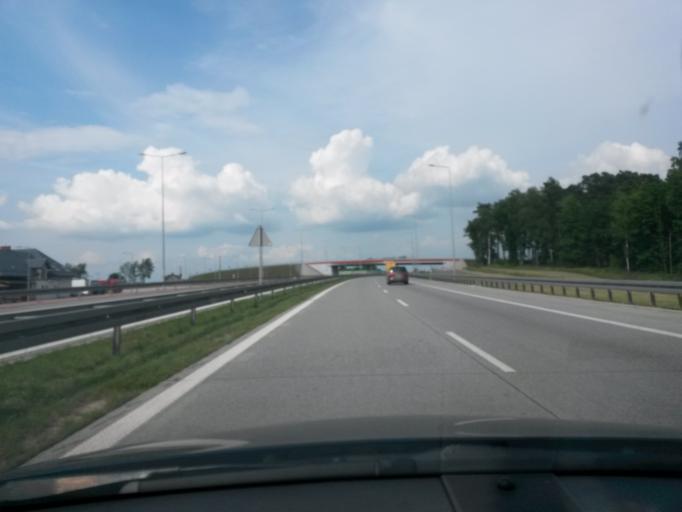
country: PL
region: Lodz Voivodeship
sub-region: Powiat tomaszowski
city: Lubochnia
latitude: 51.5883
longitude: 20.0399
